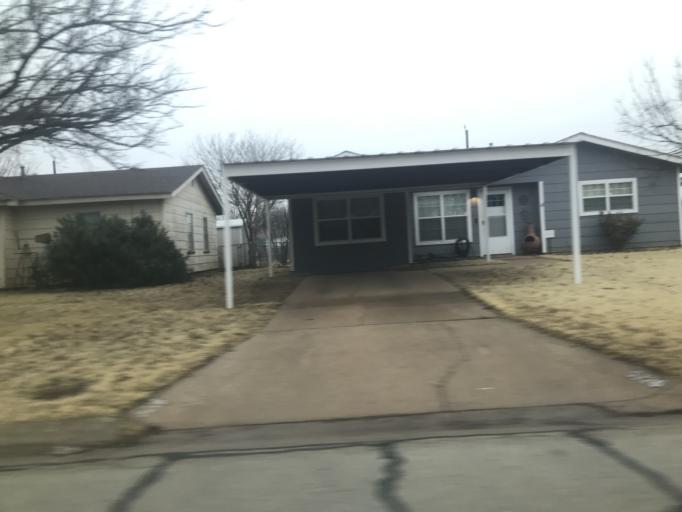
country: US
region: Texas
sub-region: Taylor County
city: Abilene
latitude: 32.4449
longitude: -99.7900
